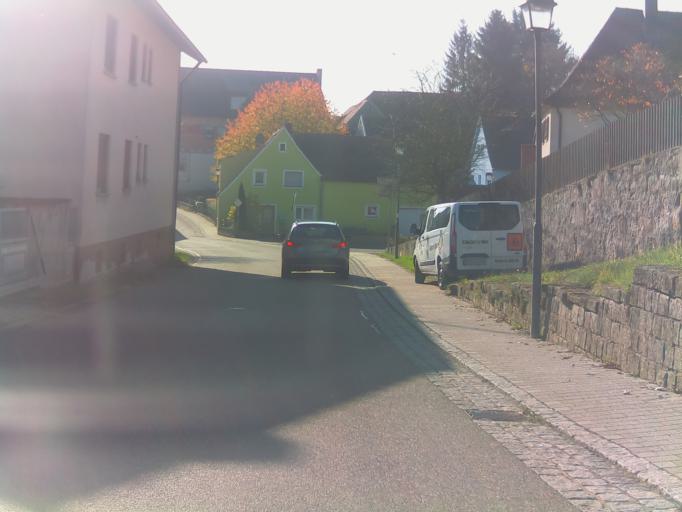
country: DE
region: Bavaria
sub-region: Regierungsbezirk Unterfranken
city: Knetzgau
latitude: 49.9060
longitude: 10.5584
